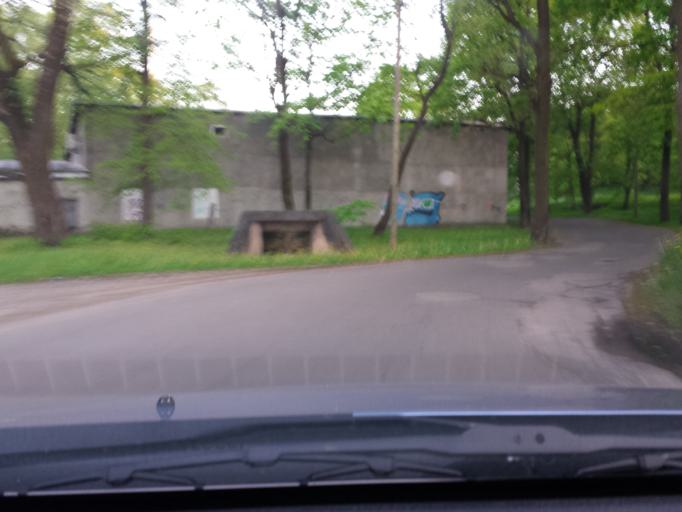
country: LV
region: Riga
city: Riga
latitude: 56.9857
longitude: 24.1379
